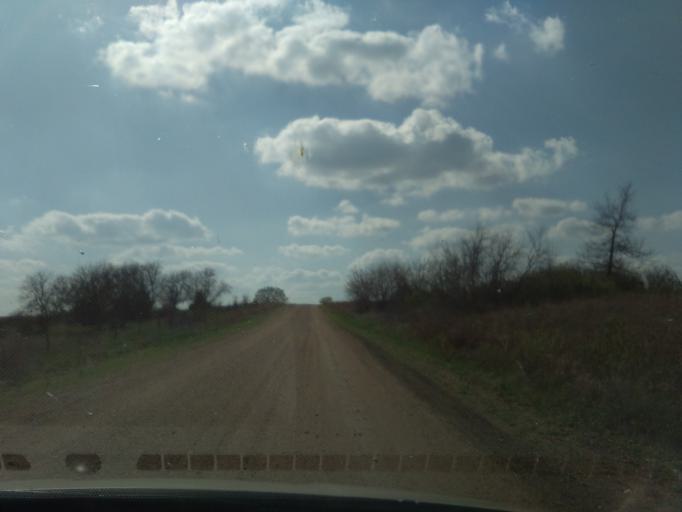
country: US
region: Nebraska
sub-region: Webster County
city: Red Cloud
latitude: 40.0025
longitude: -98.3394
